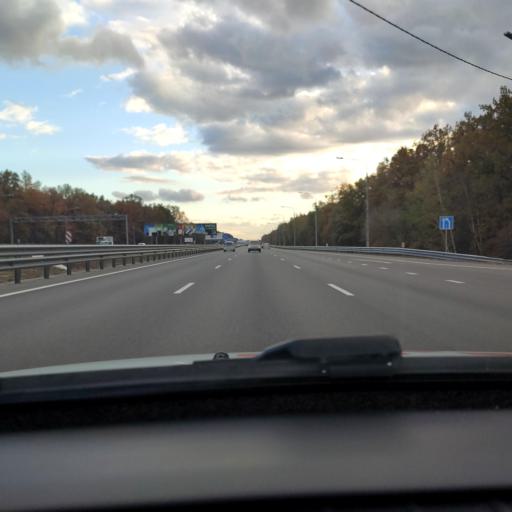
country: RU
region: Voronezj
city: Podgornoye
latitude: 51.7680
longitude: 39.1915
